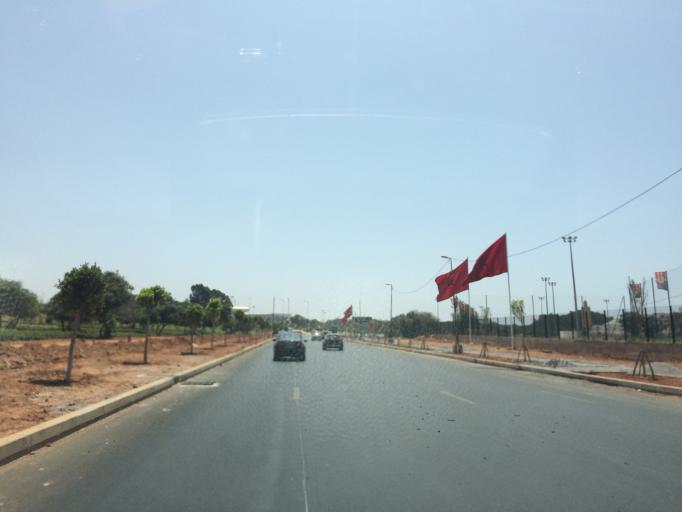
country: MA
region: Rabat-Sale-Zemmour-Zaer
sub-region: Skhirate-Temara
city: Temara
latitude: 33.9708
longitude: -6.8818
